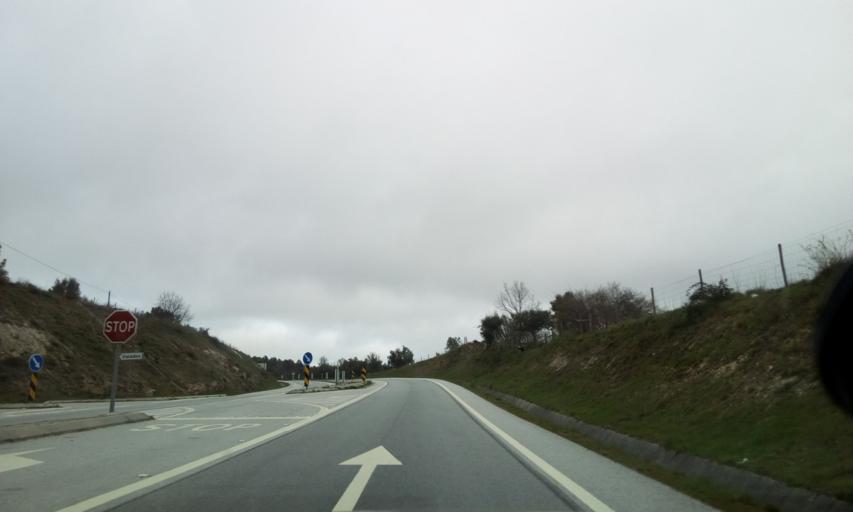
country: PT
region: Guarda
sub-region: Fornos de Algodres
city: Fornos de Algodres
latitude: 40.6268
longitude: -7.5044
